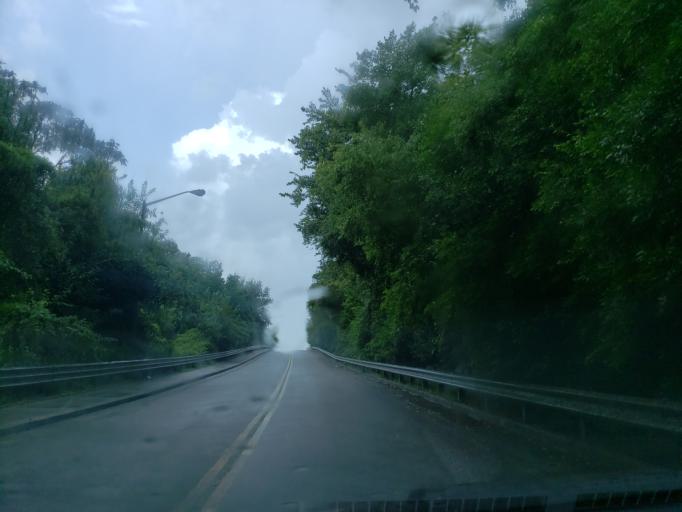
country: US
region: Georgia
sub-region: Chatham County
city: Thunderbolt
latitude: 32.0301
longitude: -81.0827
